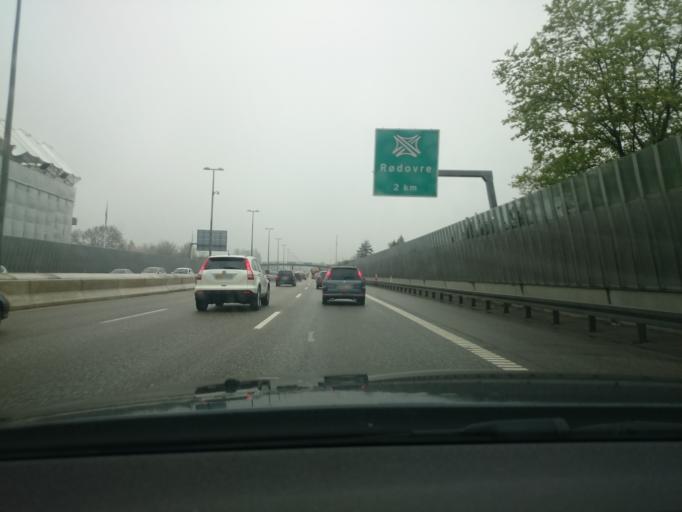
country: DK
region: Capital Region
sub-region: Herlev Kommune
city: Herlev
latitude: 55.7096
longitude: 12.4503
